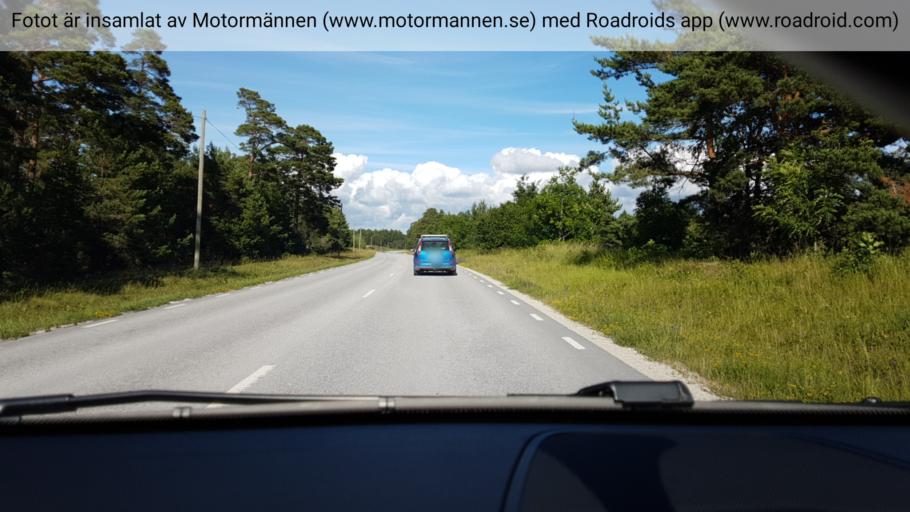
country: SE
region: Gotland
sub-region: Gotland
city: Slite
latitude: 57.7453
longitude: 18.6917
